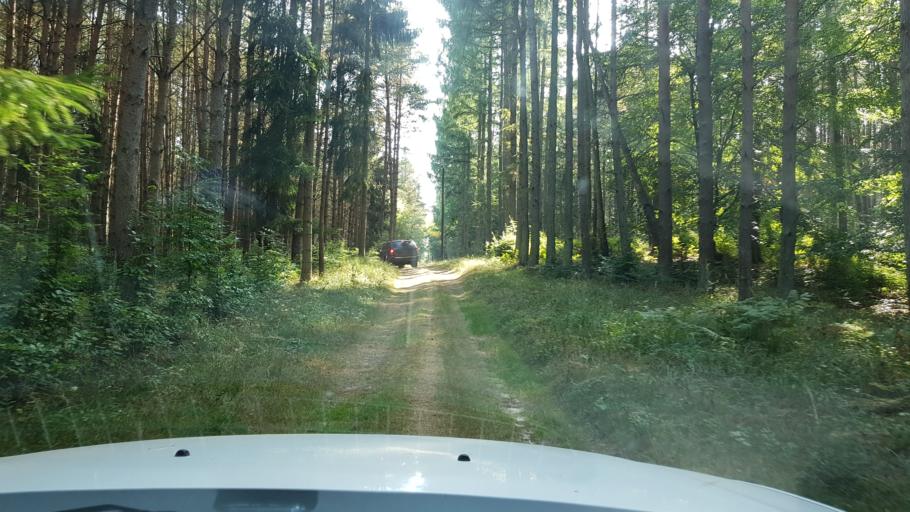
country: PL
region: West Pomeranian Voivodeship
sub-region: Powiat kamienski
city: Miedzyzdroje
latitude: 53.8747
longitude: 14.4993
